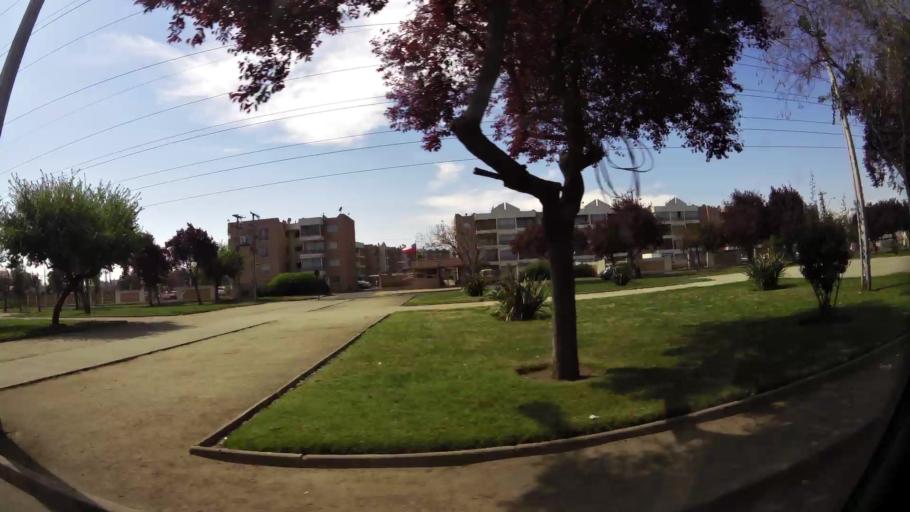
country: CL
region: Santiago Metropolitan
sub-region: Provincia de Santiago
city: Lo Prado
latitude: -33.4714
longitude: -70.7314
